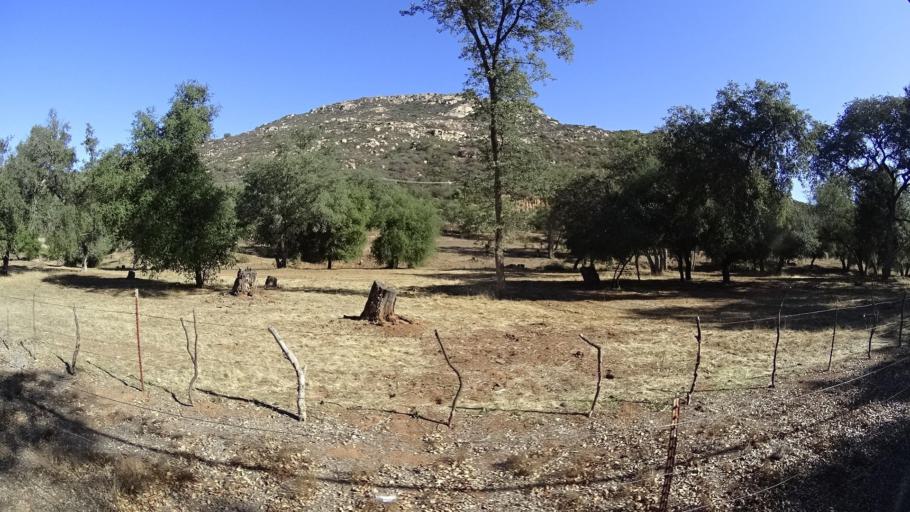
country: US
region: California
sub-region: San Diego County
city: Alpine
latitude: 32.7124
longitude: -116.7490
